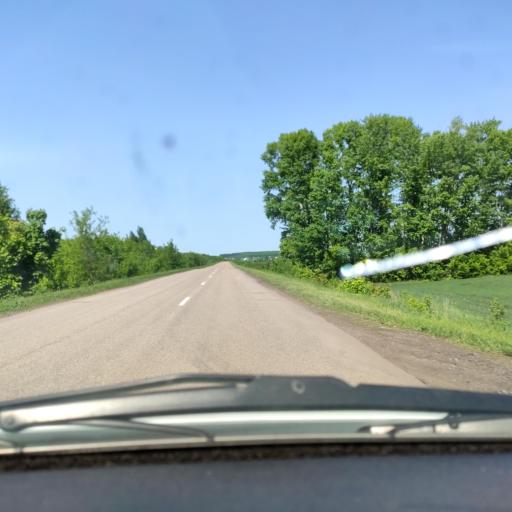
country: RU
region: Bashkortostan
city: Avdon
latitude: 54.5365
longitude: 55.6440
